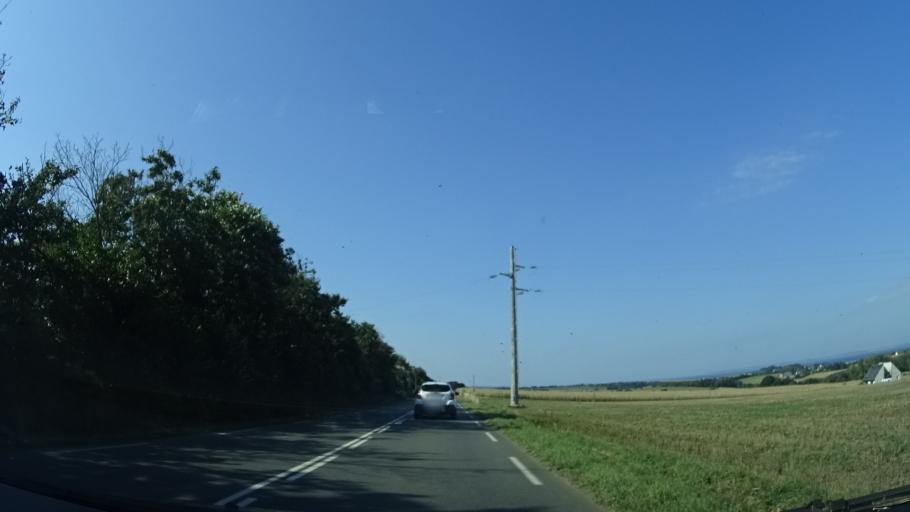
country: FR
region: Brittany
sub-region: Departement du Finistere
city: Plonevez-Porzay
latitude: 48.1207
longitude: -4.2295
